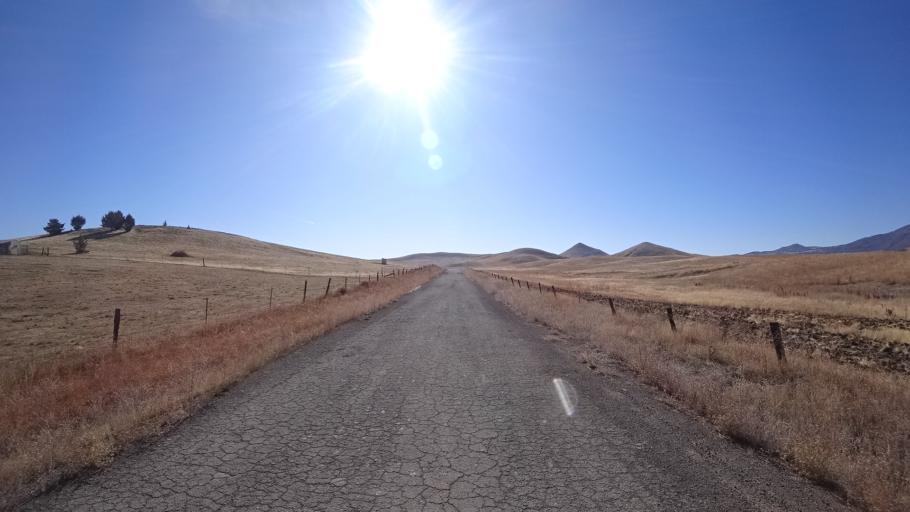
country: US
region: California
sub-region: Siskiyou County
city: Montague
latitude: 41.8472
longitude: -122.4596
